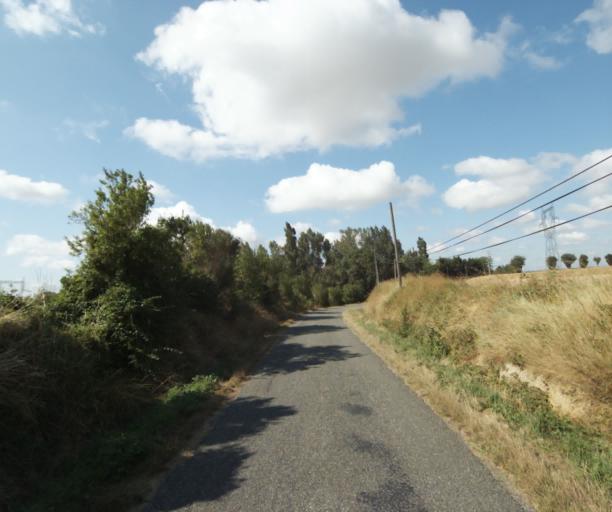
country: FR
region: Midi-Pyrenees
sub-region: Departement de la Haute-Garonne
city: Saint-Felix-Lauragais
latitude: 43.4544
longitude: 1.8352
